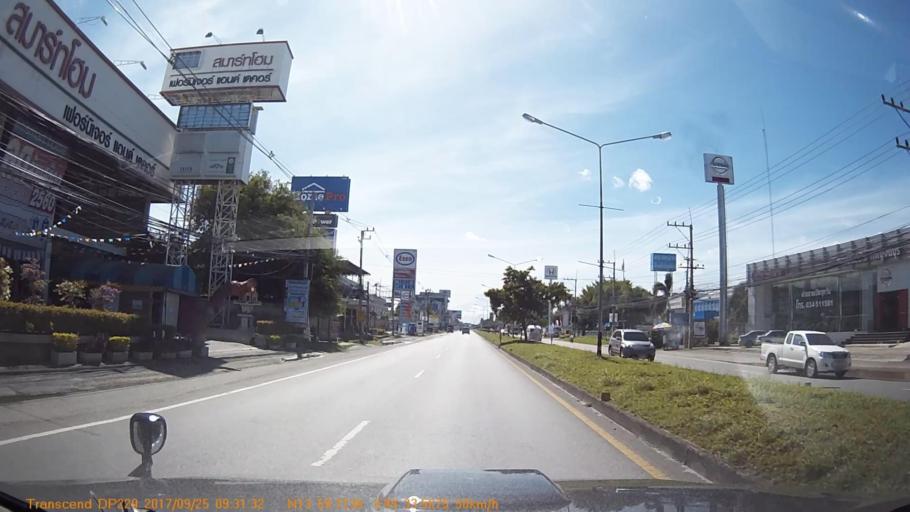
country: TH
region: Kanchanaburi
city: Kanchanaburi
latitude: 13.9951
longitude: 99.5596
